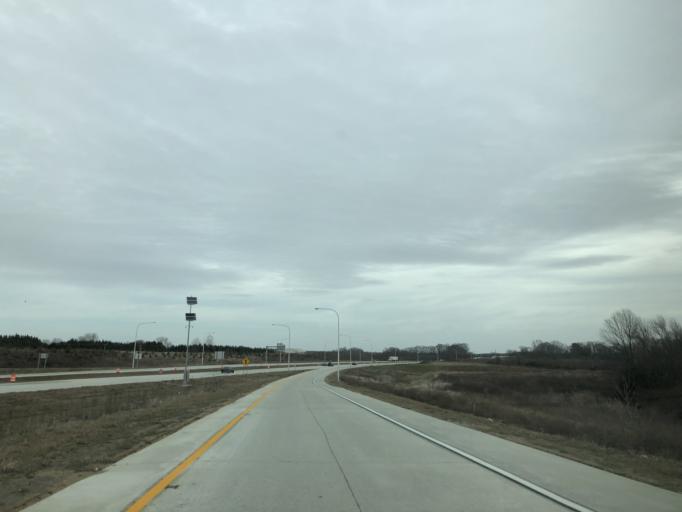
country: US
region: Delaware
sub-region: New Castle County
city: Middletown
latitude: 39.5240
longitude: -75.6768
